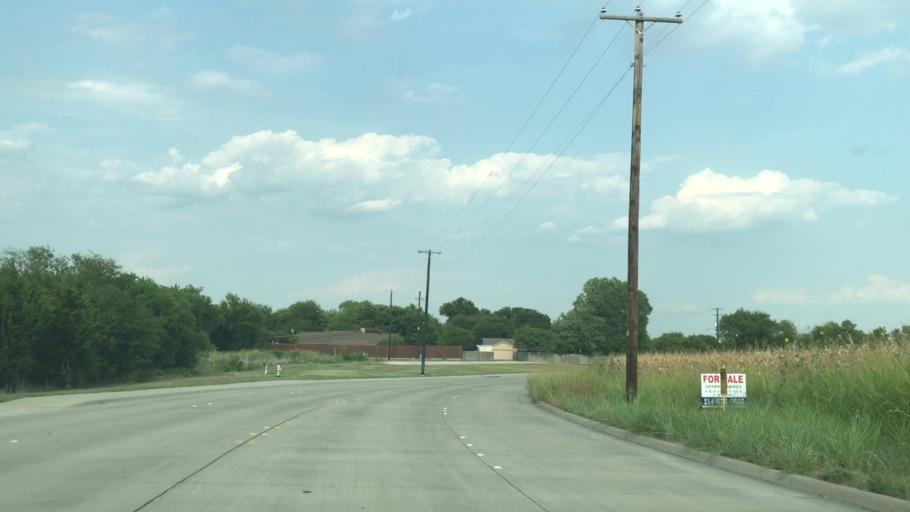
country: US
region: Texas
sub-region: Rockwall County
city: Rockwall
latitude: 32.9259
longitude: -96.4291
